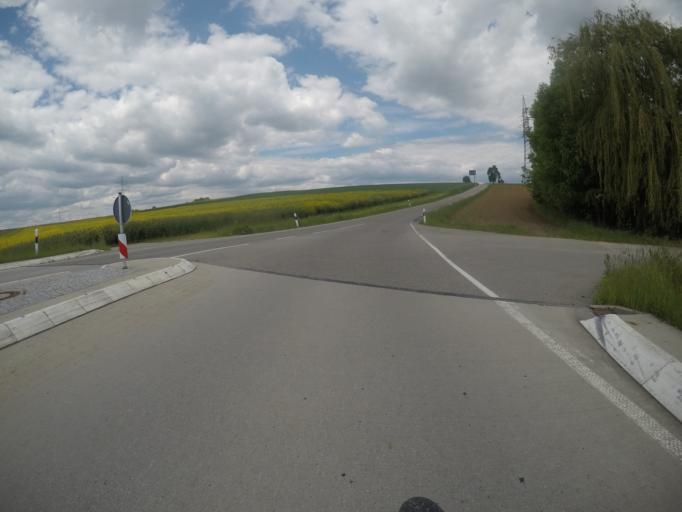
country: DE
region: Baden-Wuerttemberg
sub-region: Regierungsbezirk Stuttgart
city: Oberjettingen
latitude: 48.5797
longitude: 8.7613
